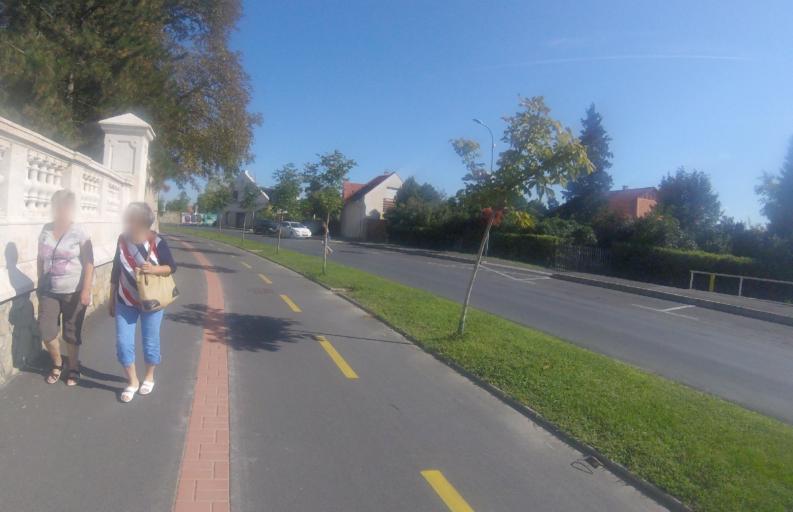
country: HU
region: Zala
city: Keszthely
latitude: 46.7708
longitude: 17.2436
